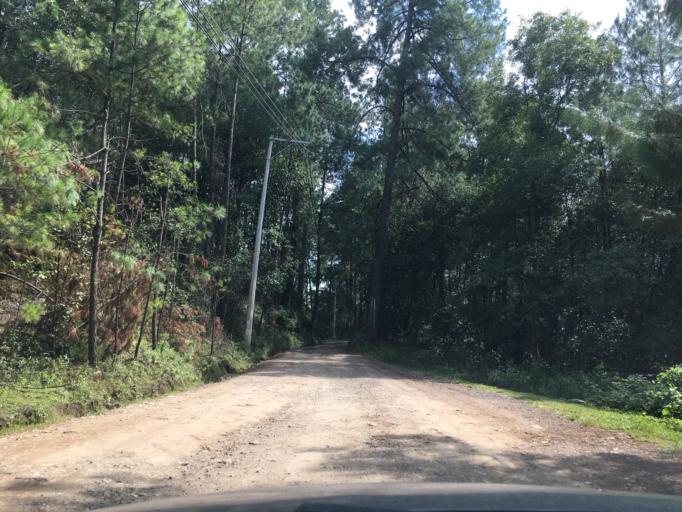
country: MX
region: Michoacan
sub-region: Morelia
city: Morelos
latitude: 19.5386
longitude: -101.1986
